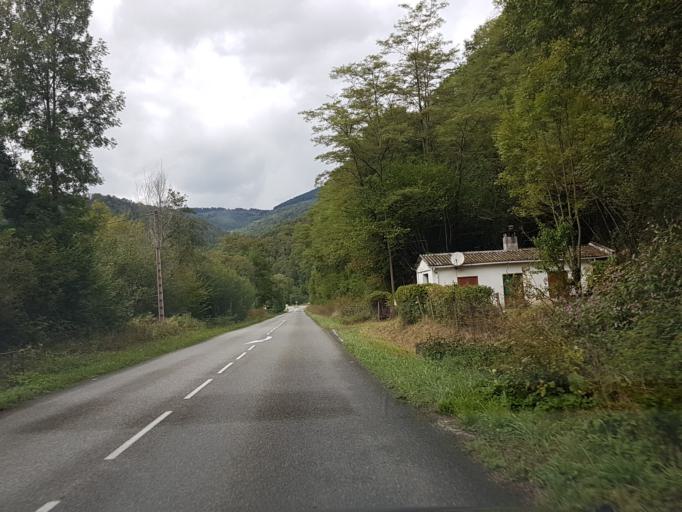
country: FR
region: Midi-Pyrenees
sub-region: Departement de l'Ariege
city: Saint-Girons
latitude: 42.8953
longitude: 1.2152
